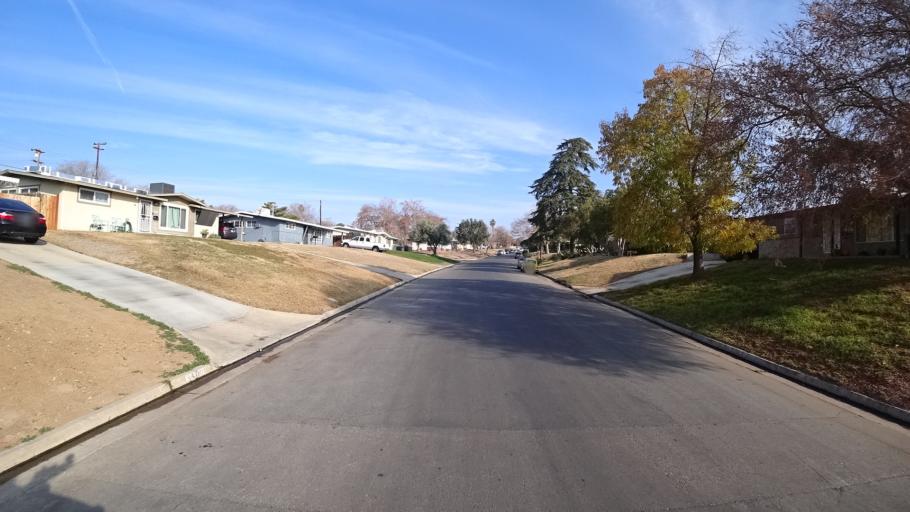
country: US
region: California
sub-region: Kern County
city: Oildale
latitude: 35.4039
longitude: -118.9816
